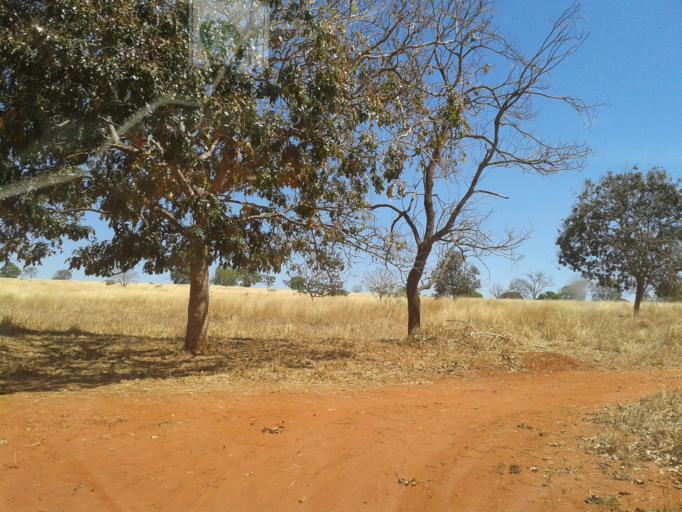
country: BR
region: Minas Gerais
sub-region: Ituiutaba
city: Ituiutaba
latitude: -19.1269
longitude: -49.3064
